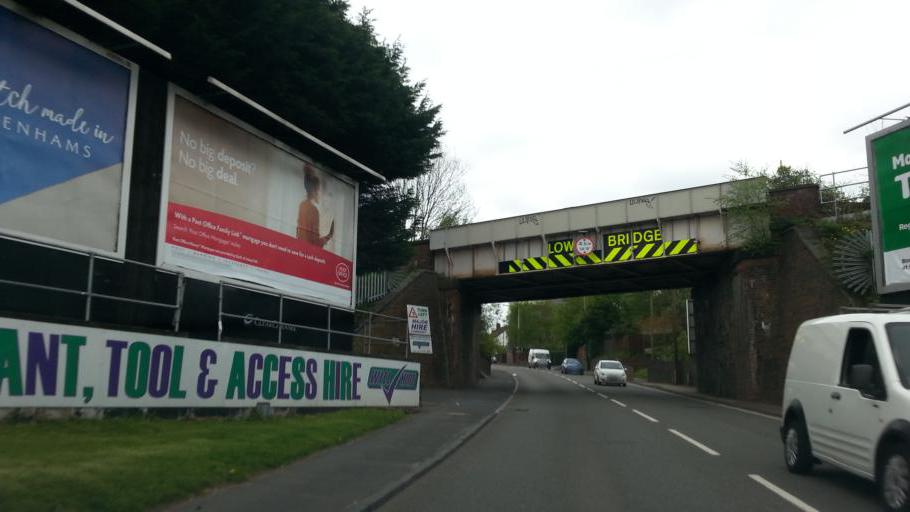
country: GB
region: England
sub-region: Dudley
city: Stourbridge
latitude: 52.4578
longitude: -2.1269
